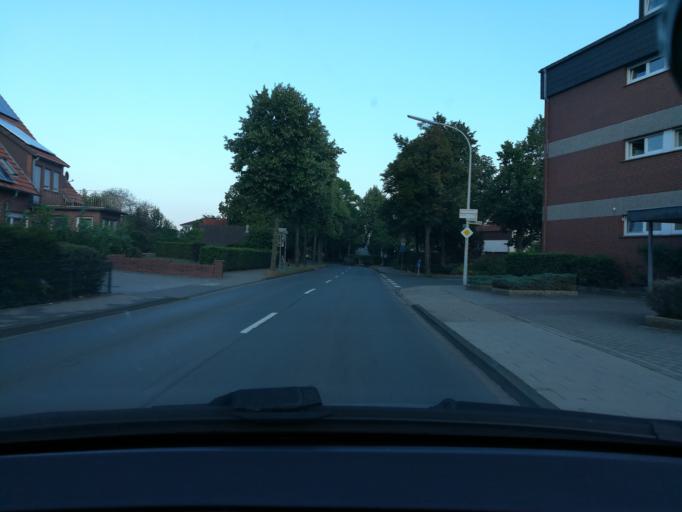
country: DE
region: North Rhine-Westphalia
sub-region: Regierungsbezirk Munster
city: Lienen
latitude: 52.1459
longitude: 7.9788
